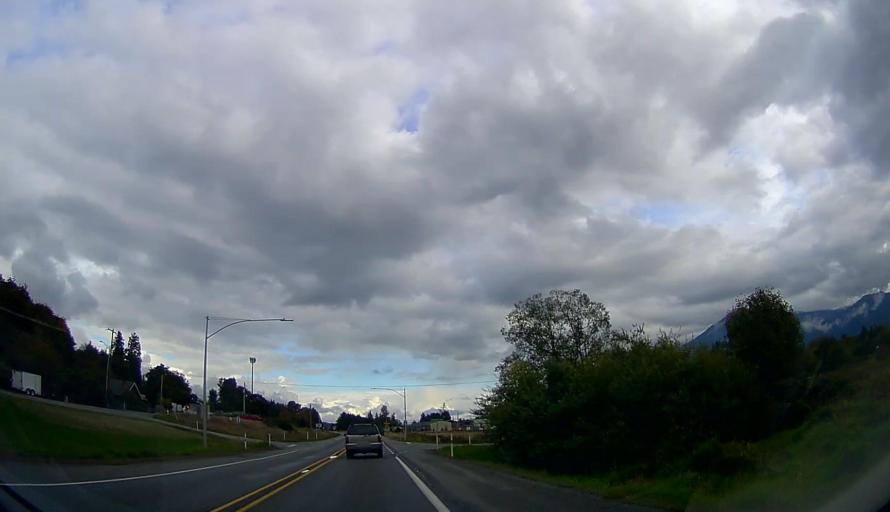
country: US
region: Washington
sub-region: Skagit County
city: Sedro-Woolley
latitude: 48.5299
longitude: -122.0612
